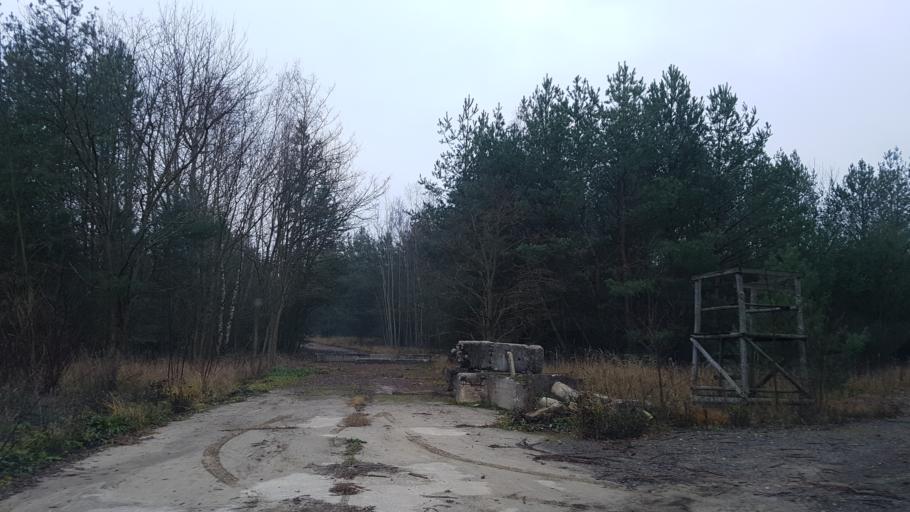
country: DE
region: Brandenburg
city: Ruckersdorf
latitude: 51.5619
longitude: 13.5765
